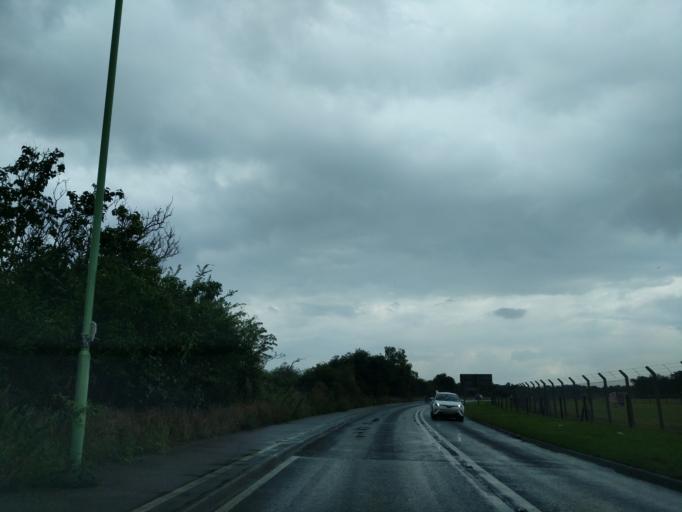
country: GB
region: England
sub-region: Suffolk
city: Lakenheath
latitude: 52.3607
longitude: 0.5141
